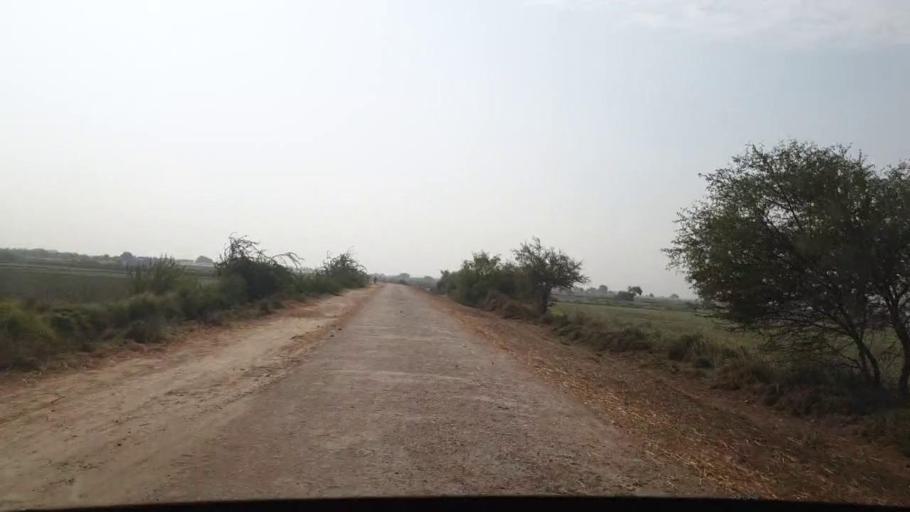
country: PK
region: Sindh
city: Chuhar Jamali
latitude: 24.3828
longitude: 67.9389
